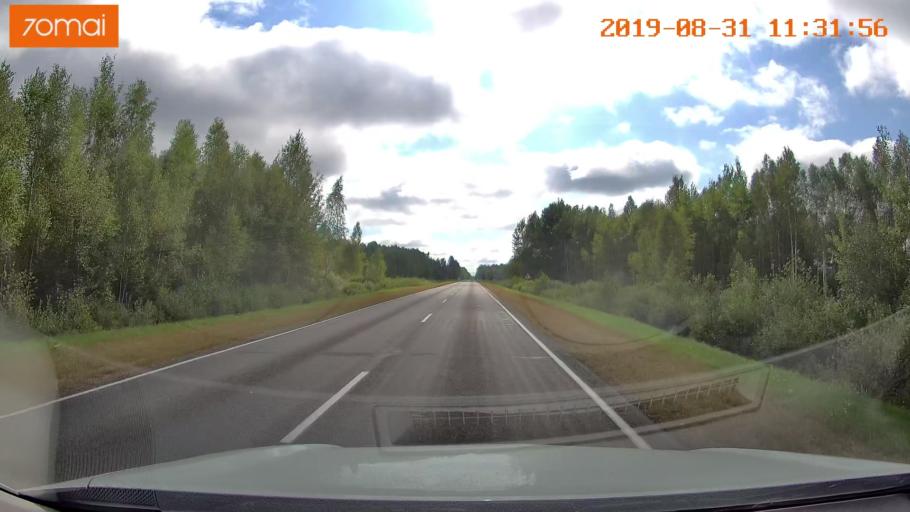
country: BY
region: Mogilev
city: Chavusy
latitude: 53.6993
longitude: 31.1541
